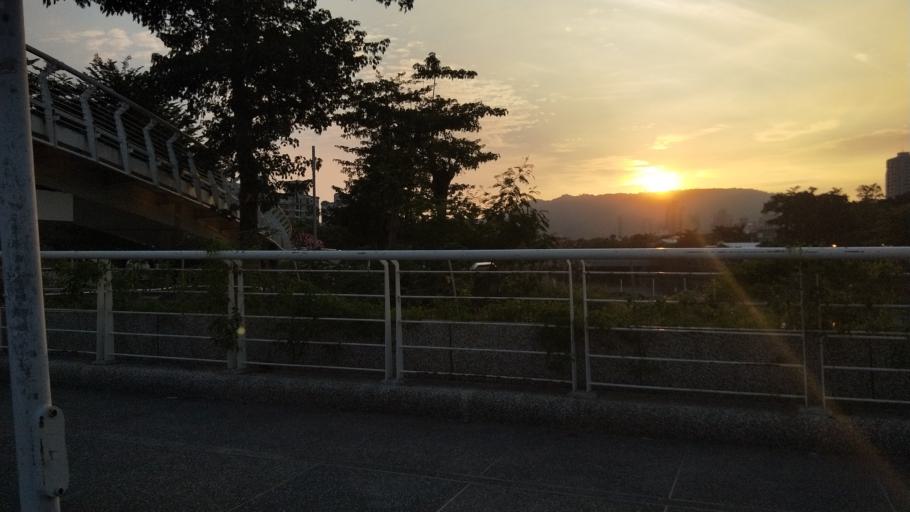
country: TW
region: Kaohsiung
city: Kaohsiung
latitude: 22.6532
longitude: 120.3036
